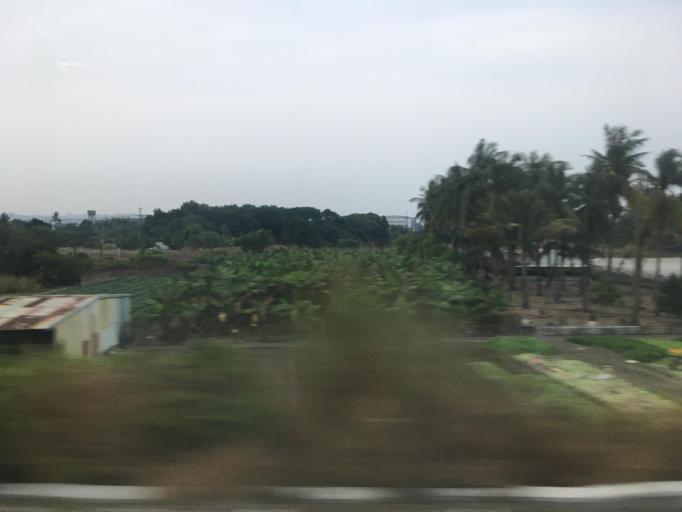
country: TW
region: Taiwan
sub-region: Pingtung
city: Pingtung
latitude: 22.6621
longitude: 120.4513
